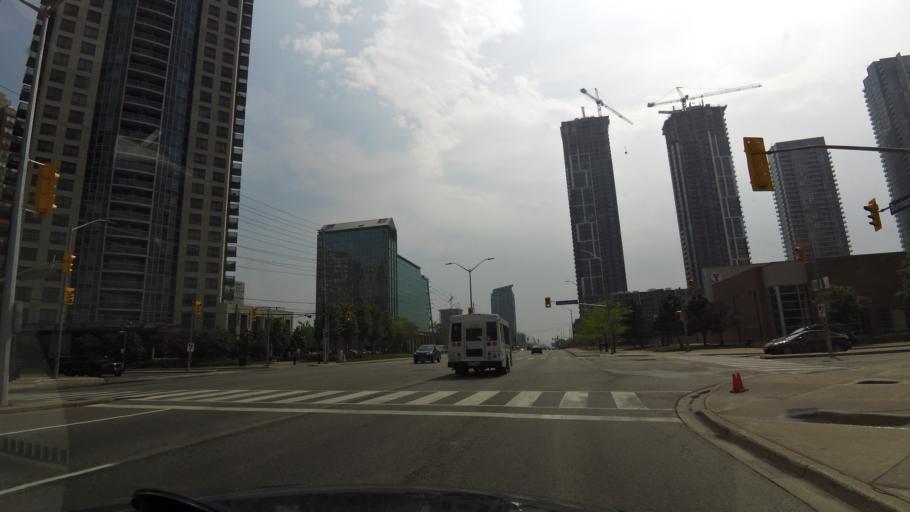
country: CA
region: Ontario
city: Mississauga
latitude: 43.5871
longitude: -79.6431
